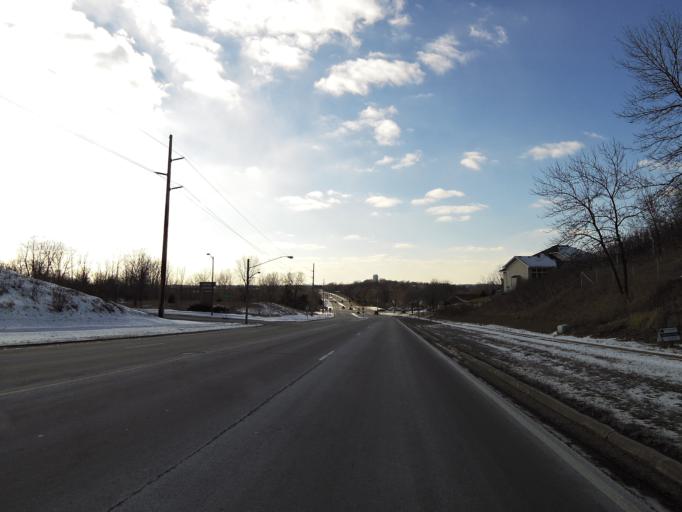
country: US
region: Minnesota
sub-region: Dakota County
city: Burnsville
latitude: 44.7537
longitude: -93.2742
